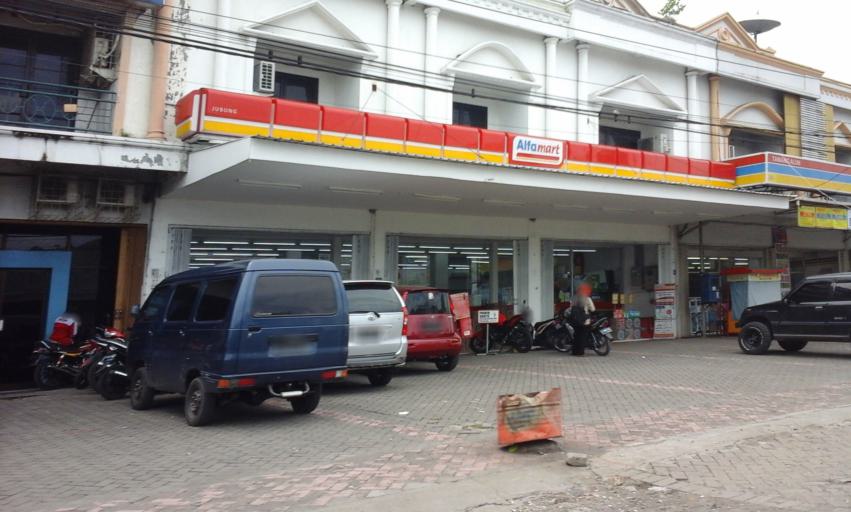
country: ID
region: East Java
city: Jubung
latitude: -8.1971
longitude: 113.6340
